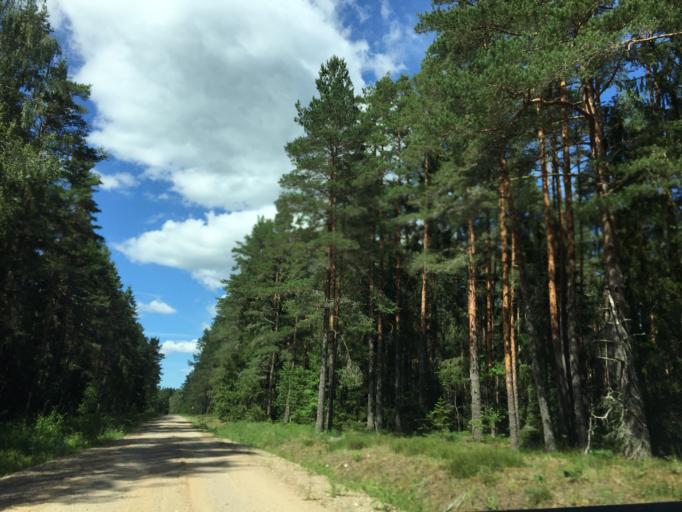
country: LV
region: Kuldigas Rajons
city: Kuldiga
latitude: 57.1038
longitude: 21.8919
